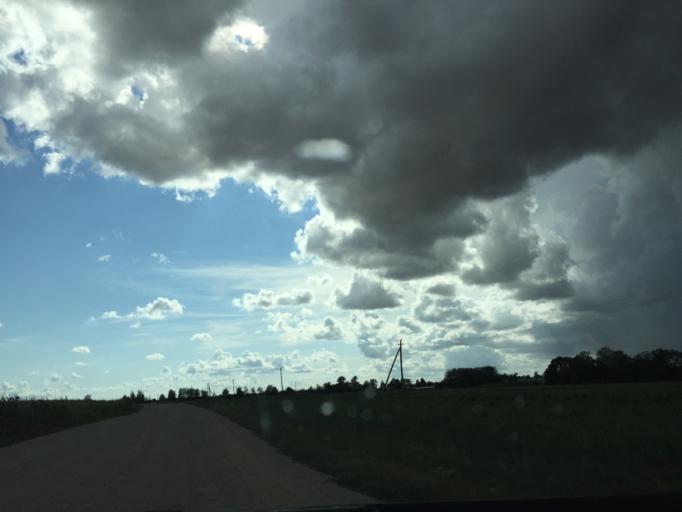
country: LV
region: Tervete
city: Zelmeni
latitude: 56.3046
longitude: 23.4174
